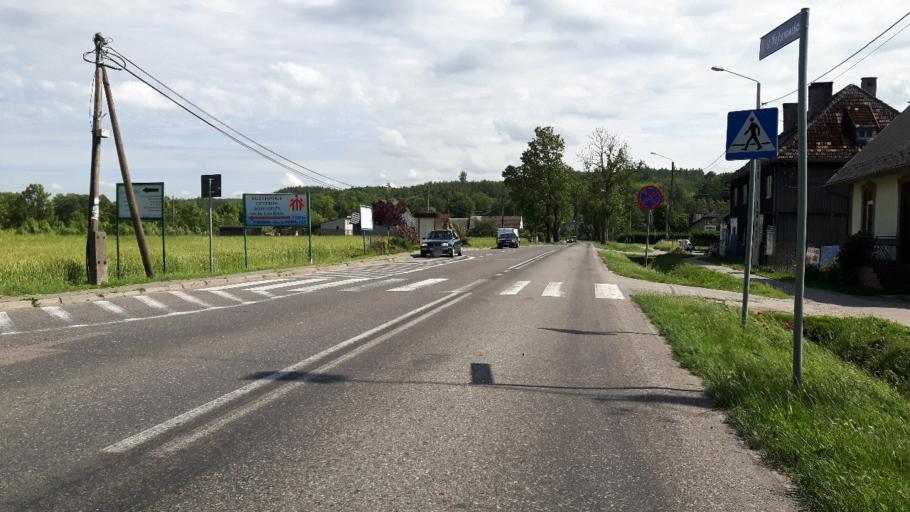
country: PL
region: Pomeranian Voivodeship
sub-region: Powiat wejherowski
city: Orle
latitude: 54.6526
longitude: 18.0999
